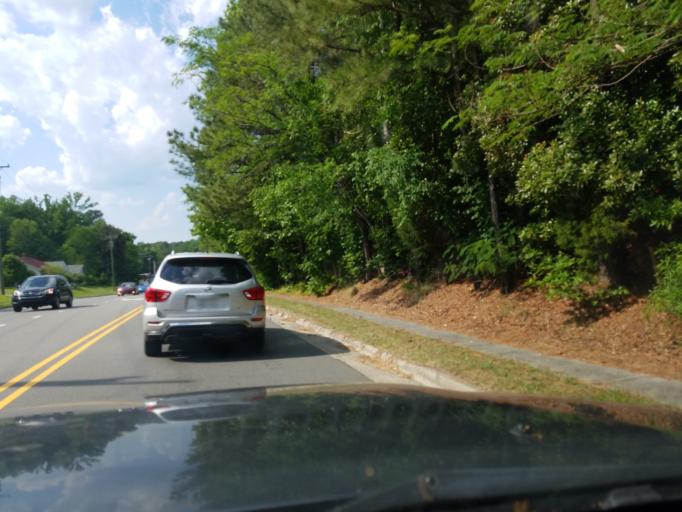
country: US
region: North Carolina
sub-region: Durham County
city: Durham
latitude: 35.9459
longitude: -78.9680
